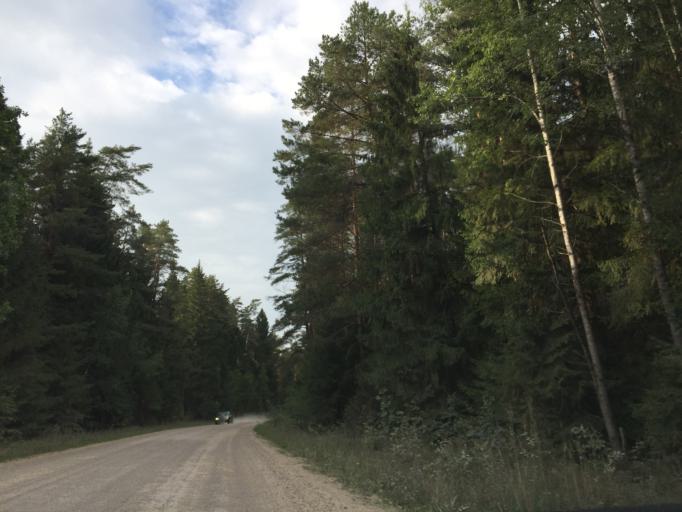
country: LV
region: Baldone
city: Baldone
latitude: 56.7932
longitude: 24.4392
